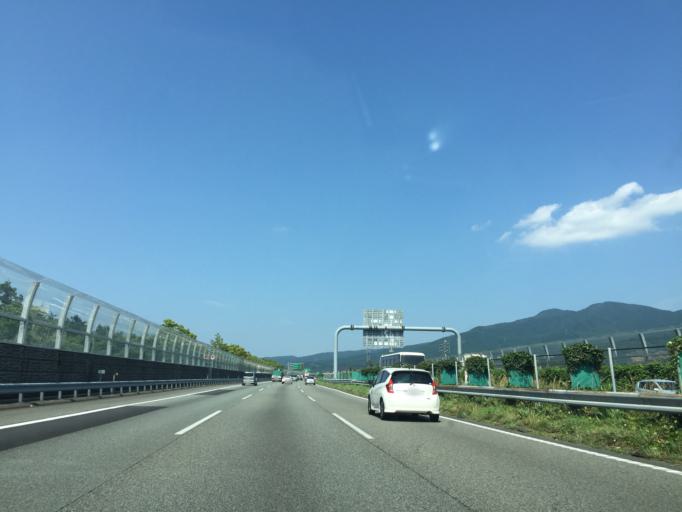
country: JP
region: Shizuoka
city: Gotemba
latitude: 35.2878
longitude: 138.9316
